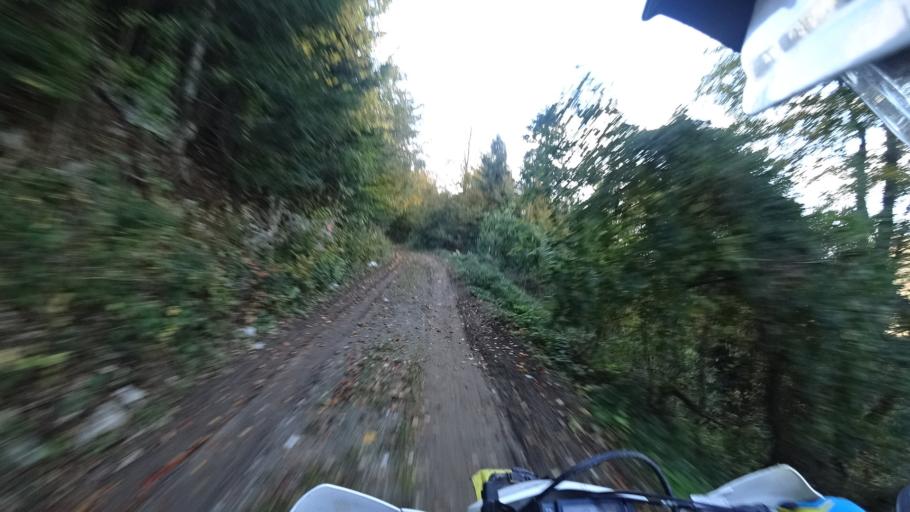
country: HR
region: Karlovacka
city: Plaski
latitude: 45.0308
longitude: 15.3818
